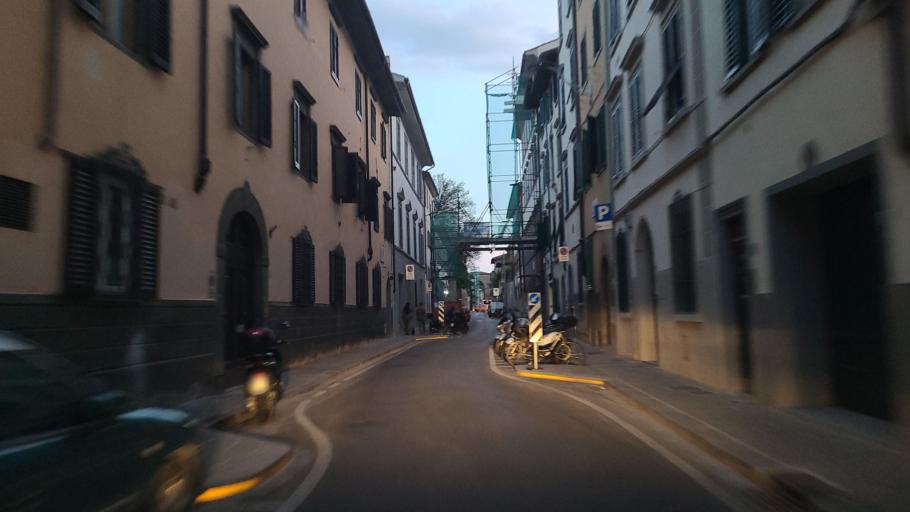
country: IT
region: Tuscany
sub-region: Province of Florence
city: Florence
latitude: 43.7648
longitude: 11.2440
